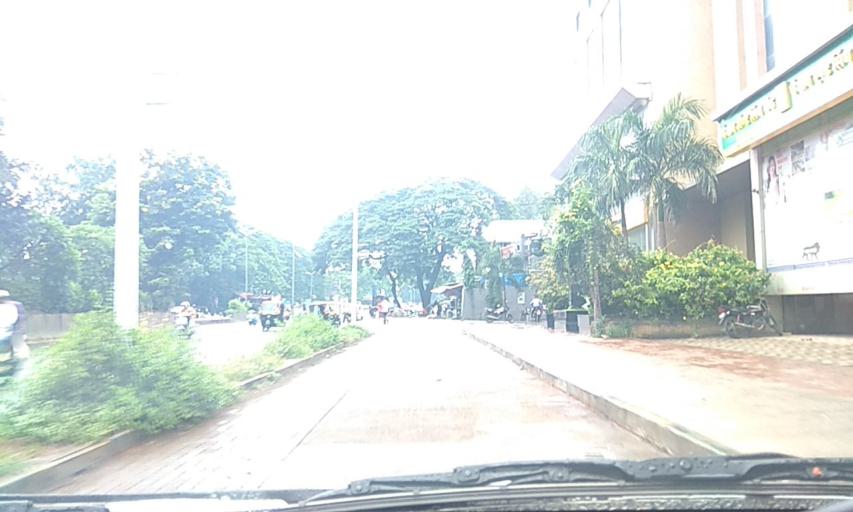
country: IN
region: Maharashtra
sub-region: Pune Division
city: Shivaji Nagar
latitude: 18.5353
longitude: 73.8514
